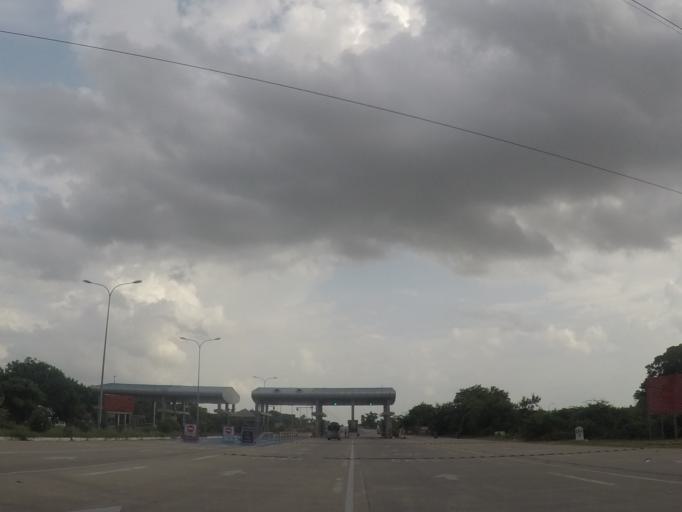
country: MM
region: Mandalay
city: Meiktila
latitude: 20.8145
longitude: 95.7685
